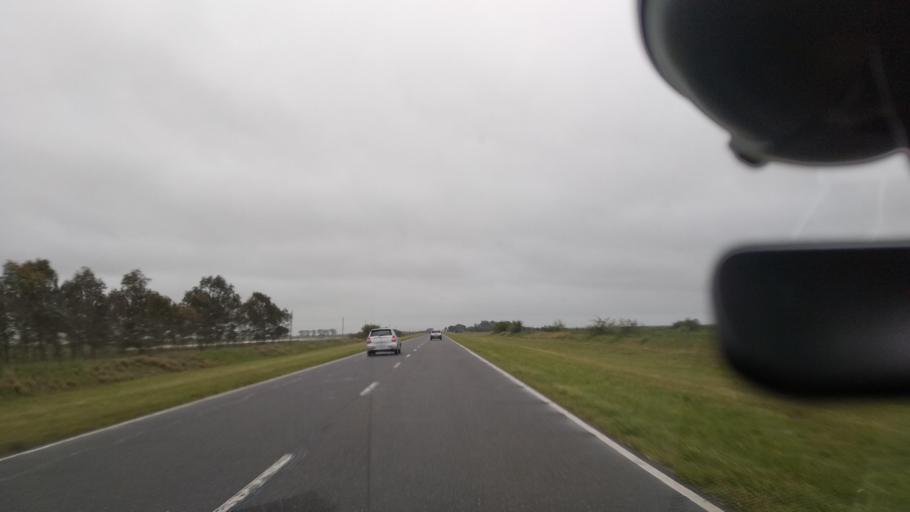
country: AR
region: Buenos Aires
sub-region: Partido de Dolores
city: Dolores
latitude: -36.0676
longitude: -57.4407
